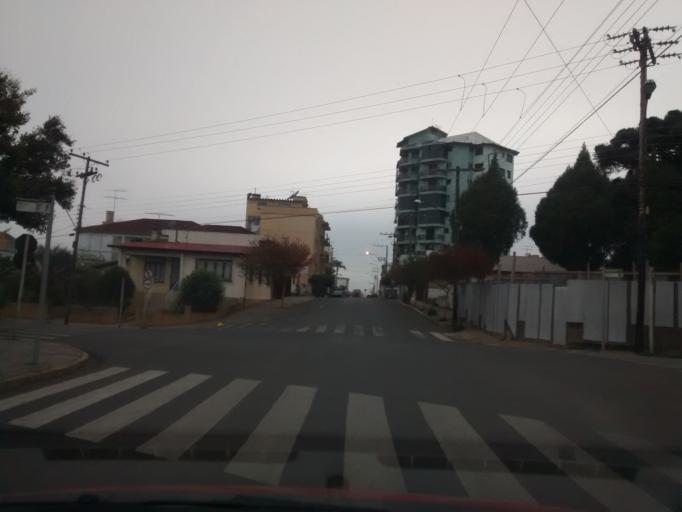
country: BR
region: Rio Grande do Sul
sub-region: Vacaria
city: Vacaria
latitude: -28.5073
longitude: -50.9382
